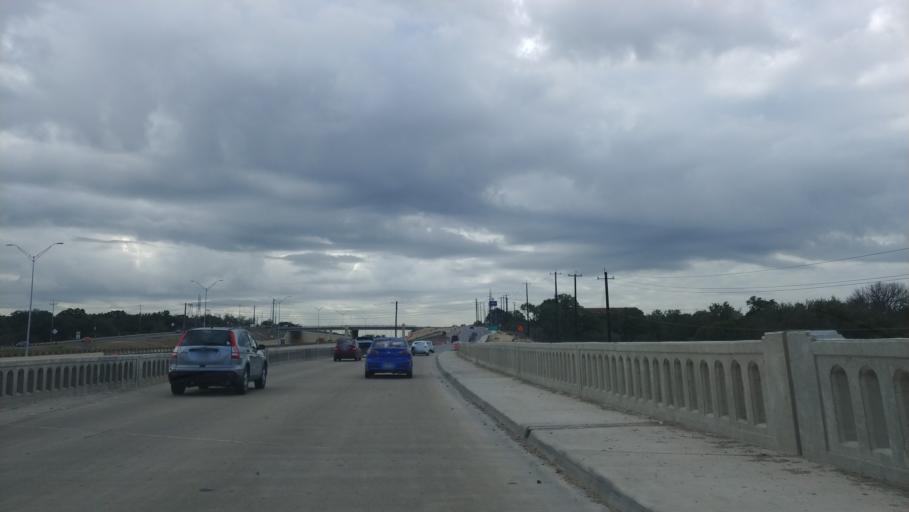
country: US
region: Texas
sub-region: Bexar County
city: Lackland Air Force Base
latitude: 29.4210
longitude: -98.7103
